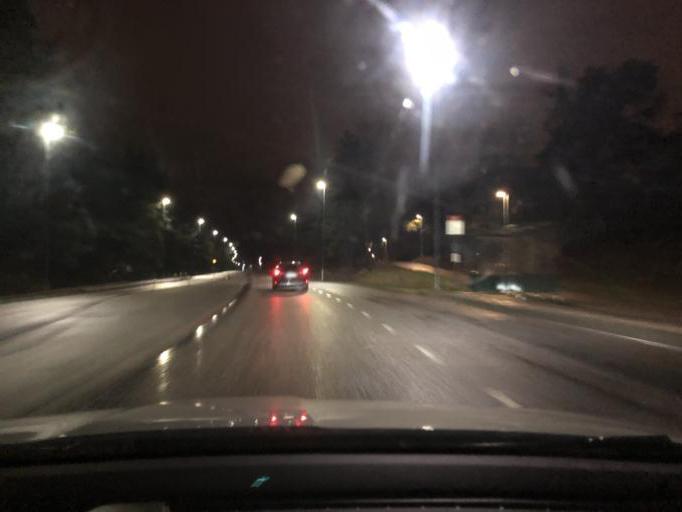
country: SE
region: Stockholm
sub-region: Jarfalla Kommun
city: Jakobsberg
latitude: 59.4047
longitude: 17.8208
